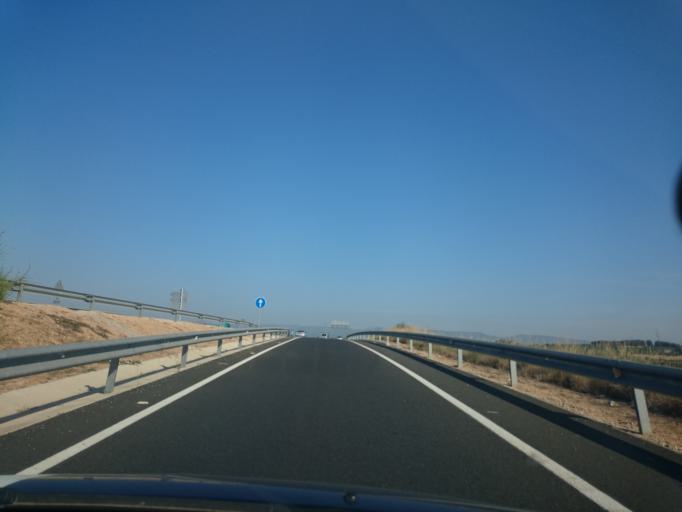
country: ES
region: Catalonia
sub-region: Provincia de Barcelona
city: La Granada
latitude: 41.3675
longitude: 1.7151
